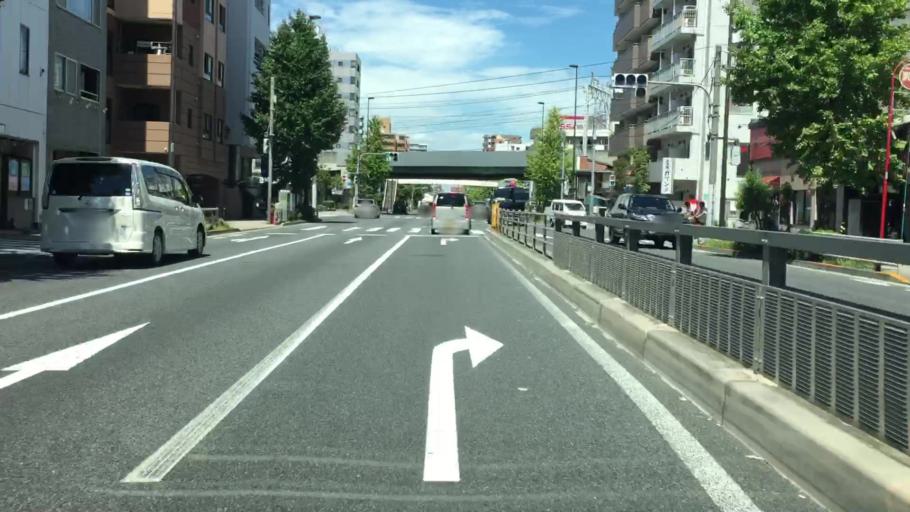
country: JP
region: Saitama
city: Soka
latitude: 35.7683
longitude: 139.8035
